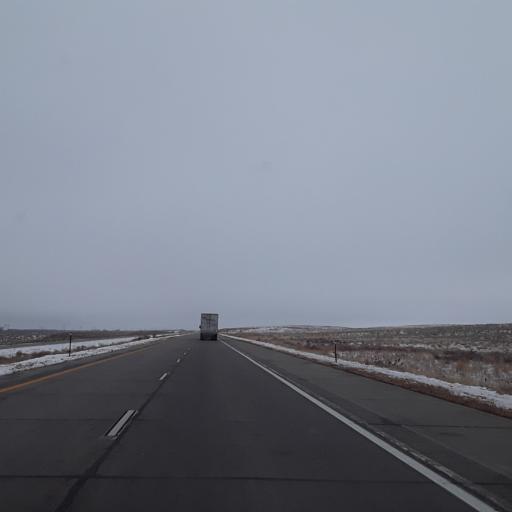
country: US
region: Colorado
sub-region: Logan County
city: Sterling
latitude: 40.5698
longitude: -103.2050
